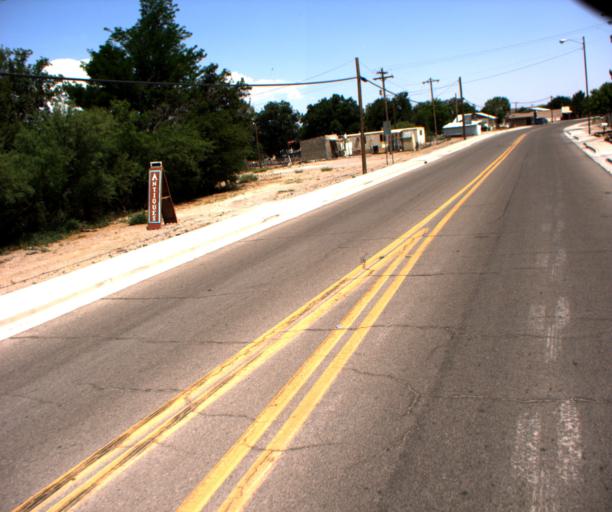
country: US
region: Arizona
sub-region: Greenlee County
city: Clifton
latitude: 32.7167
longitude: -109.1022
